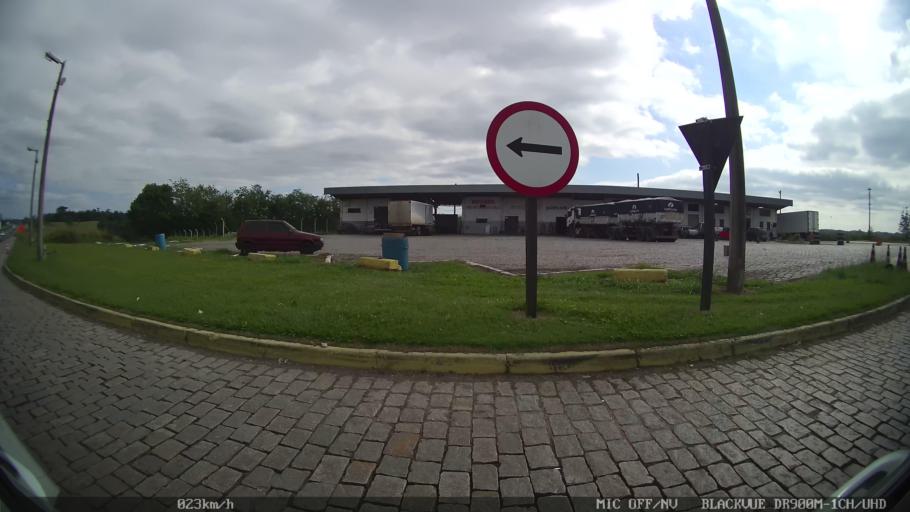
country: BR
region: Sao Paulo
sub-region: Pariquera-Acu
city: Pariquera Acu
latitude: -24.6276
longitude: -47.9013
